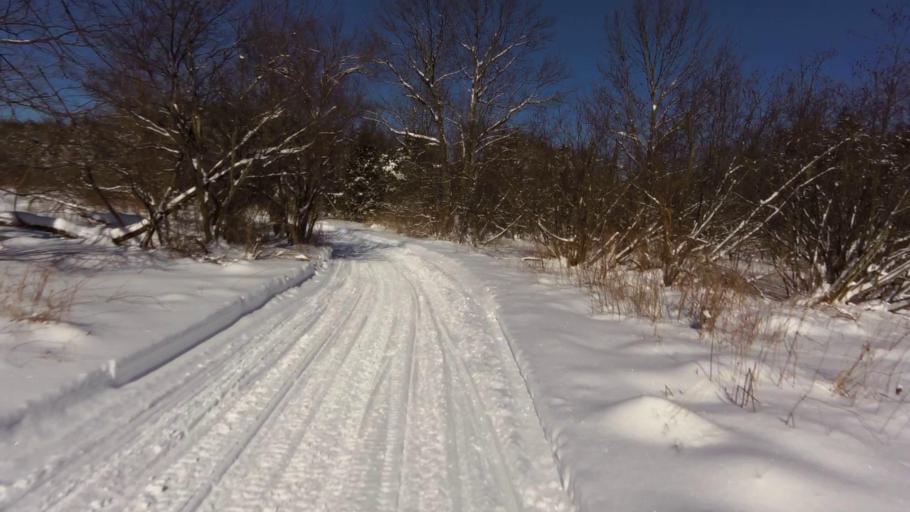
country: US
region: New York
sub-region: Chautauqua County
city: Silver Creek
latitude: 42.3729
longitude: -79.1539
